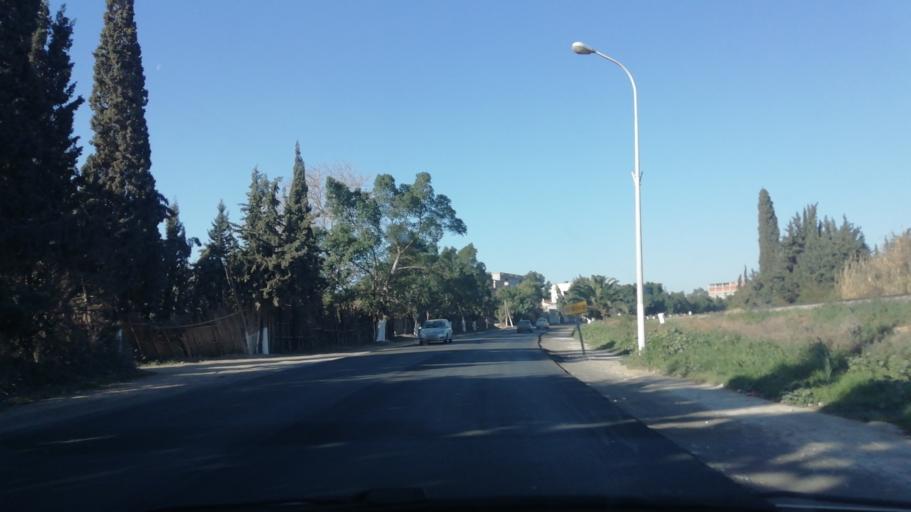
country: DZ
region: Mascara
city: Mascara
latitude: 35.5828
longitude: 0.0489
